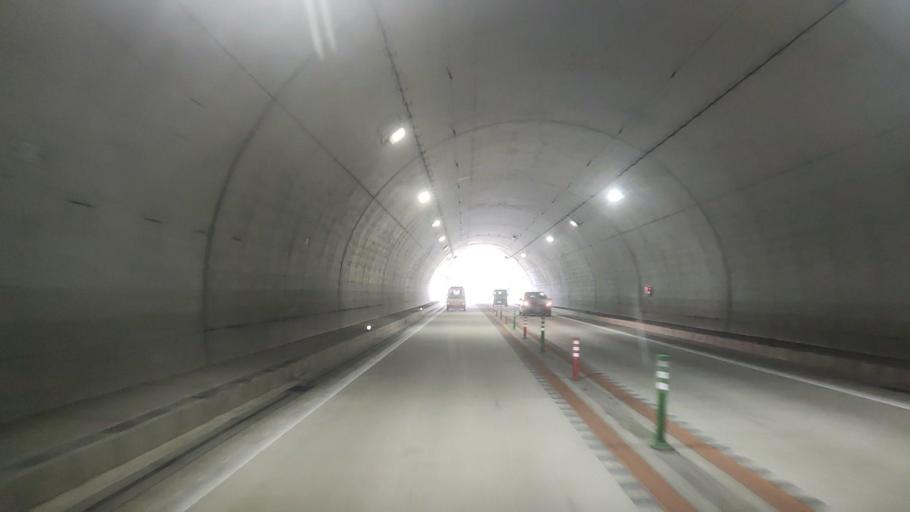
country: JP
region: Wakayama
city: Tanabe
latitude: 33.6429
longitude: 135.4098
